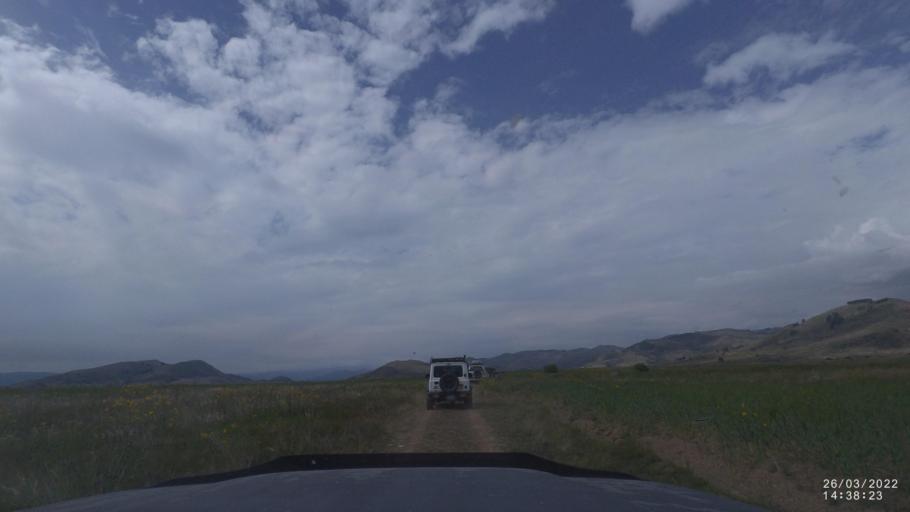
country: BO
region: Cochabamba
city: Cliza
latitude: -17.7374
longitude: -65.8621
